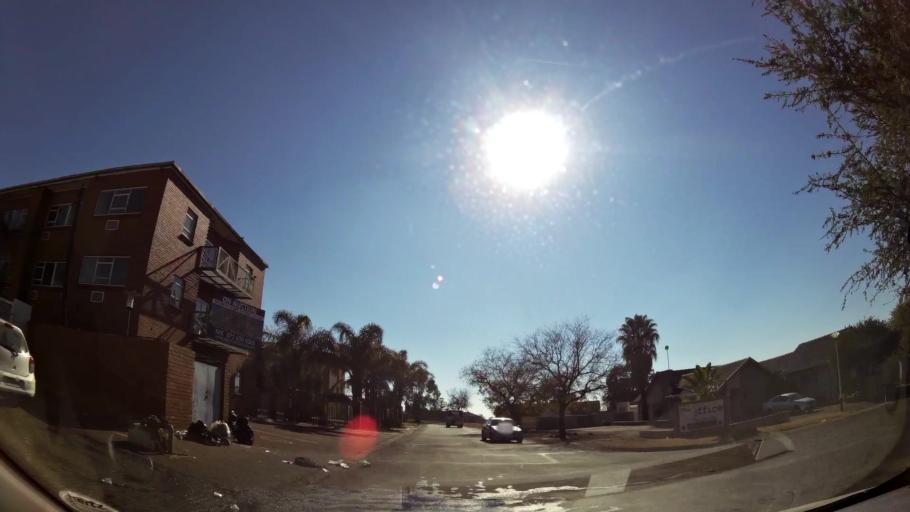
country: ZA
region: Mpumalanga
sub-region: Nkangala District Municipality
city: Witbank
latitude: -25.8745
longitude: 29.2405
